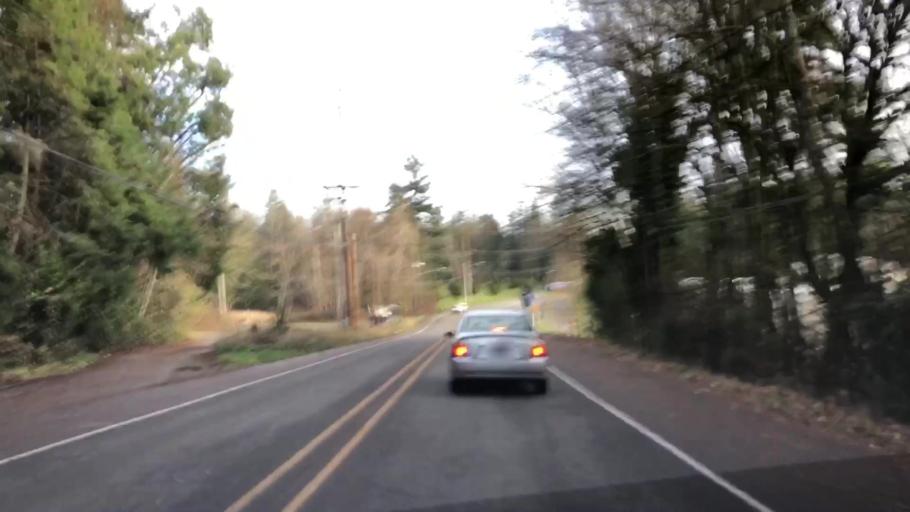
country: US
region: Washington
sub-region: Kitsap County
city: Suquamish
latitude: 47.7277
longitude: -122.5616
